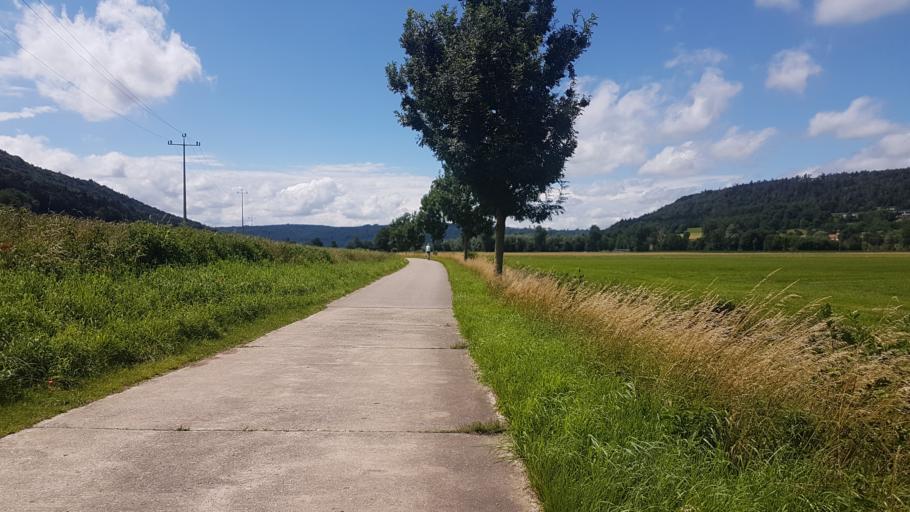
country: DE
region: Bavaria
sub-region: Upper Palatinate
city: Dietfurt
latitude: 49.0171
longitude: 11.5115
